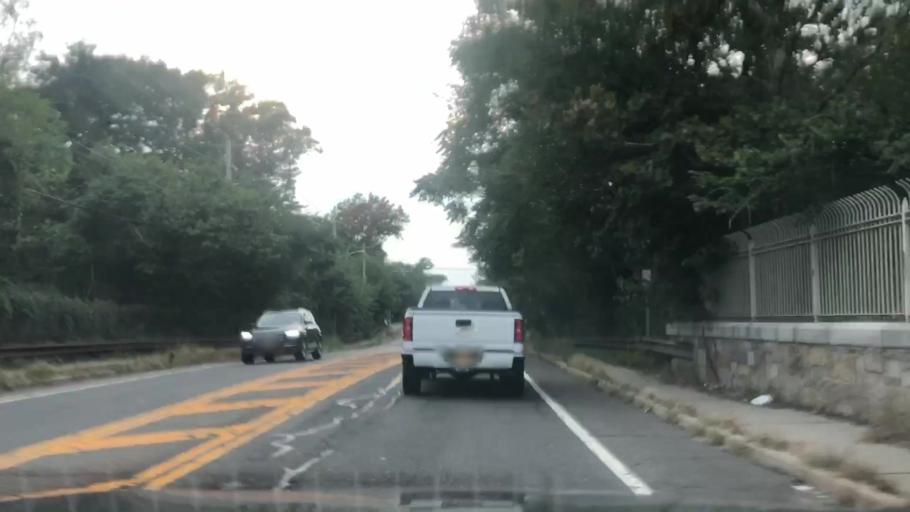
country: US
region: New York
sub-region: Nassau County
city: North Wantagh
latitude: 40.6922
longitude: -73.5190
